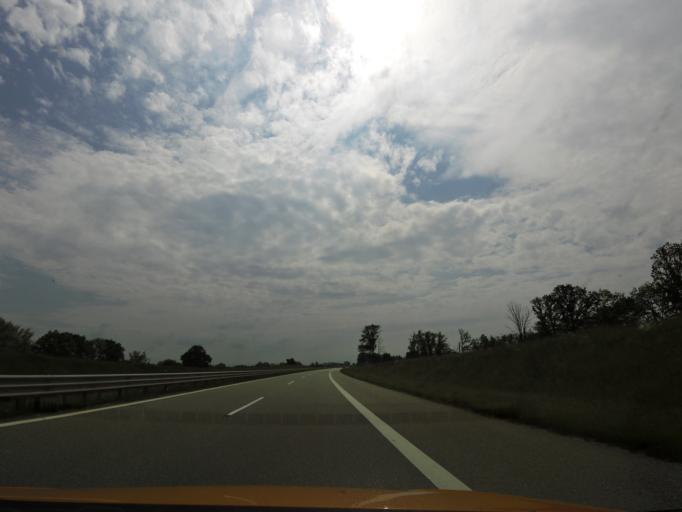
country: DE
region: Mecklenburg-Vorpommern
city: Retgendorf
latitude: 53.7475
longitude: 11.5842
